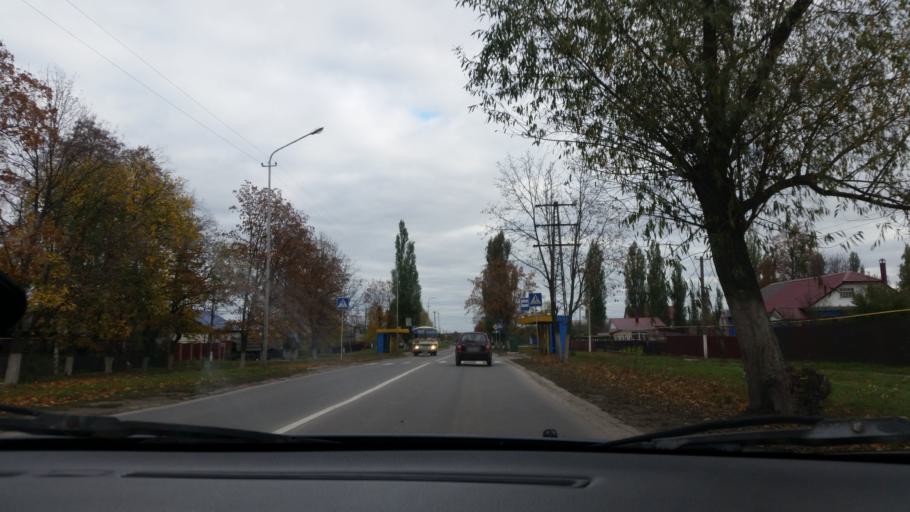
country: RU
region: Lipetsk
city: Gryazi
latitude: 52.4820
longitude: 39.9505
